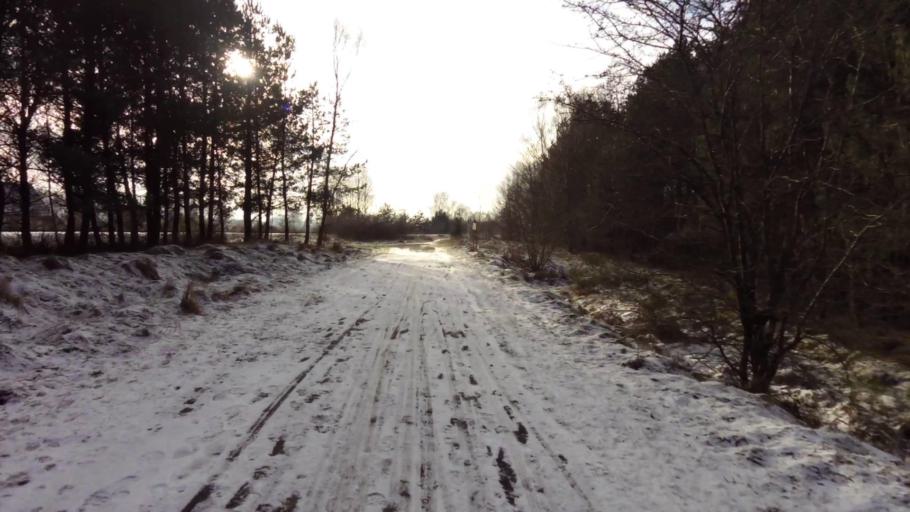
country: PL
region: West Pomeranian Voivodeship
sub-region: Powiat drawski
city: Zlocieniec
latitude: 53.5479
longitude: 16.0179
